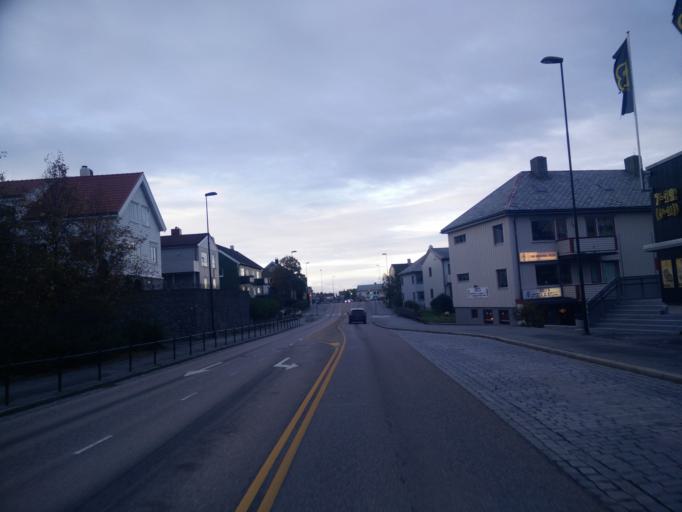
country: NO
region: More og Romsdal
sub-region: Kristiansund
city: Kristiansund
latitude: 63.1190
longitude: 7.7231
